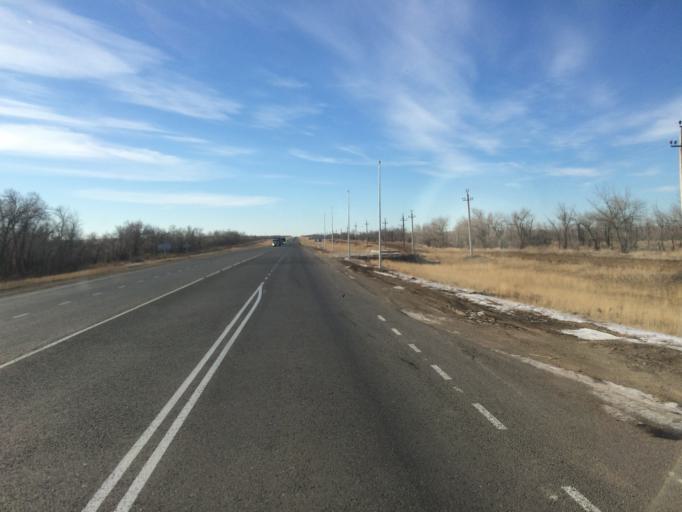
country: KZ
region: Aqtoebe
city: Aqtobe
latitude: 50.2639
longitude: 56.9518
